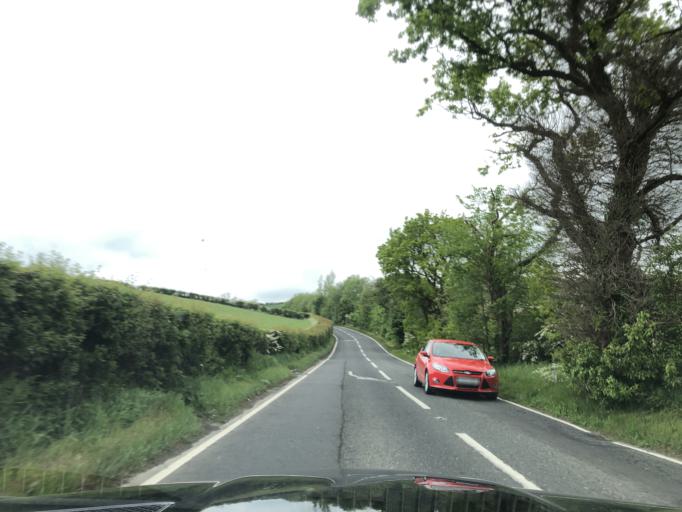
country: GB
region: Northern Ireland
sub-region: Down District
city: Downpatrick
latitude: 54.3548
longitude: -5.7407
